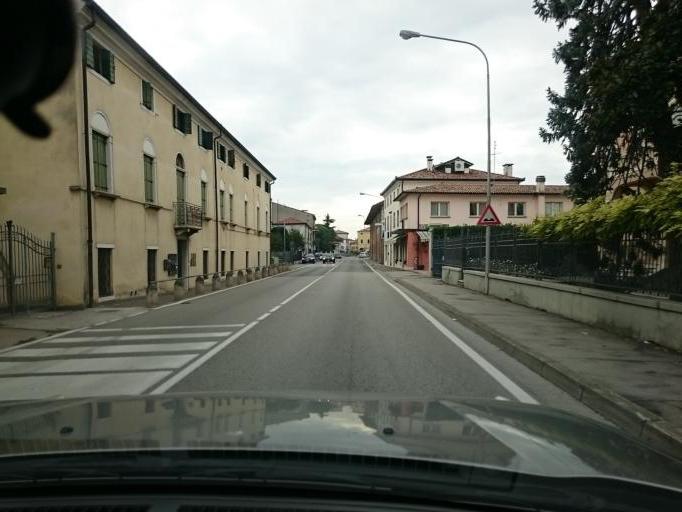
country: IT
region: Veneto
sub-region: Provincia di Padova
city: Piove di Sacco-Piovega
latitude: 45.2996
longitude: 12.0310
